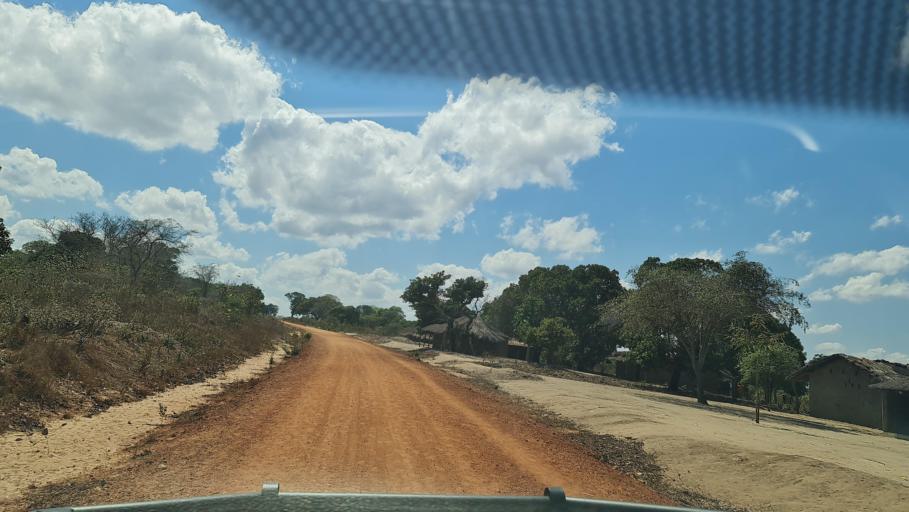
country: MZ
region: Nampula
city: Nacala
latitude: -14.1760
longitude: 40.2105
